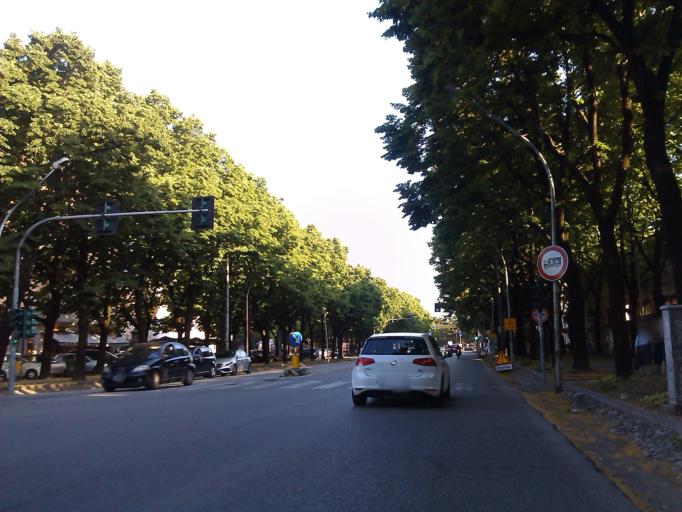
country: IT
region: Veneto
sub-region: Provincia di Vicenza
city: Bassano del Grappa
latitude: 45.7685
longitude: 11.7383
